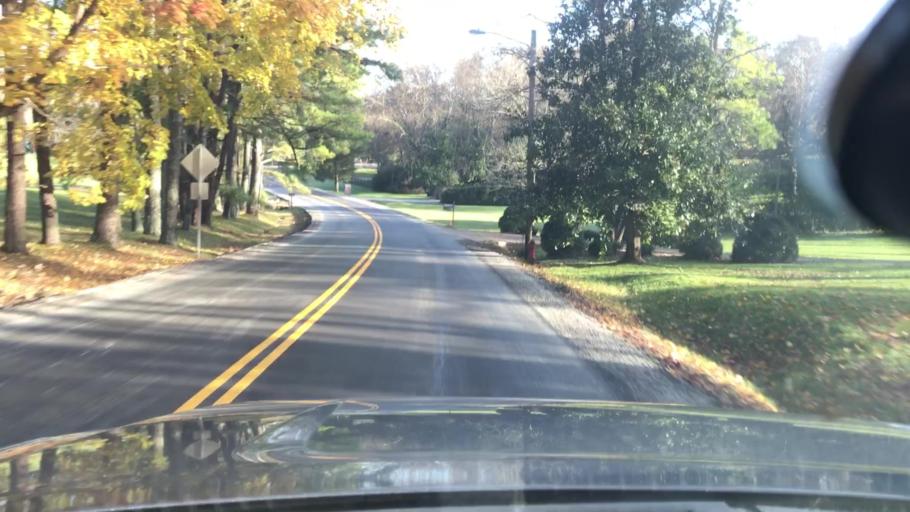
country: US
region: Tennessee
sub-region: Davidson County
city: Belle Meade
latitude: 36.1012
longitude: -86.8843
